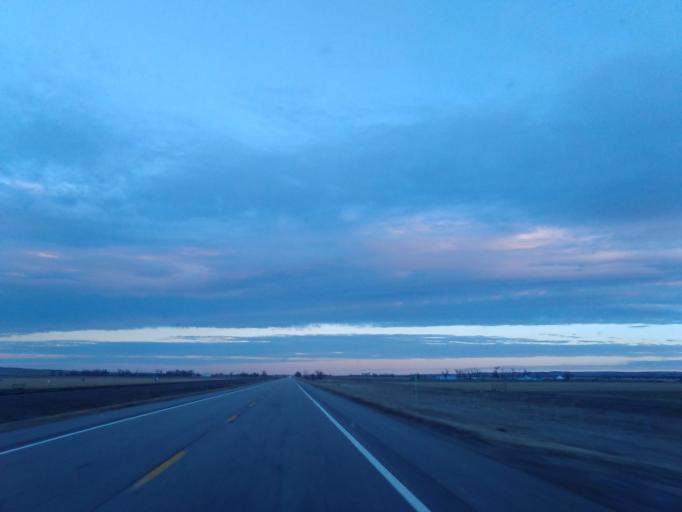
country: US
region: Nebraska
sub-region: Garden County
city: Oshkosh
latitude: 41.4004
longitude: -102.3282
